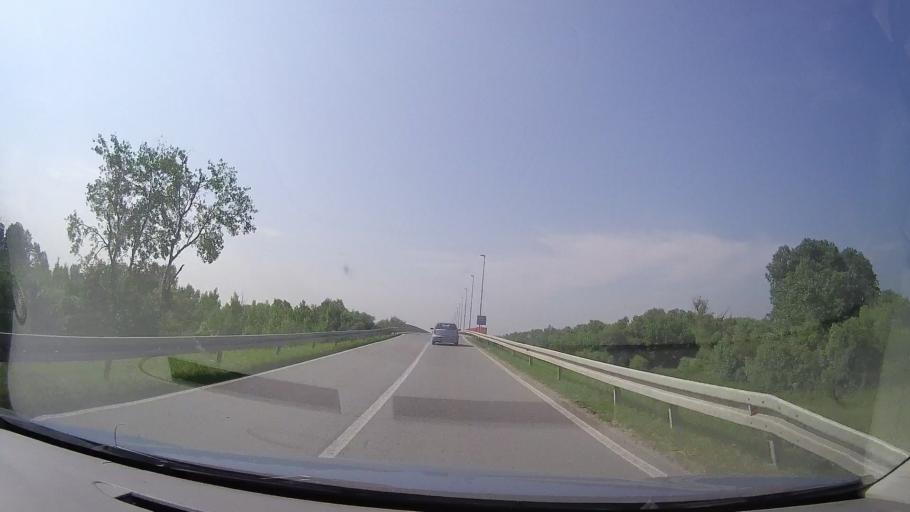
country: RS
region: Autonomna Pokrajina Vojvodina
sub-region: Srednjebanatski Okrug
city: Secanj
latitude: 45.3591
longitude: 20.7709
